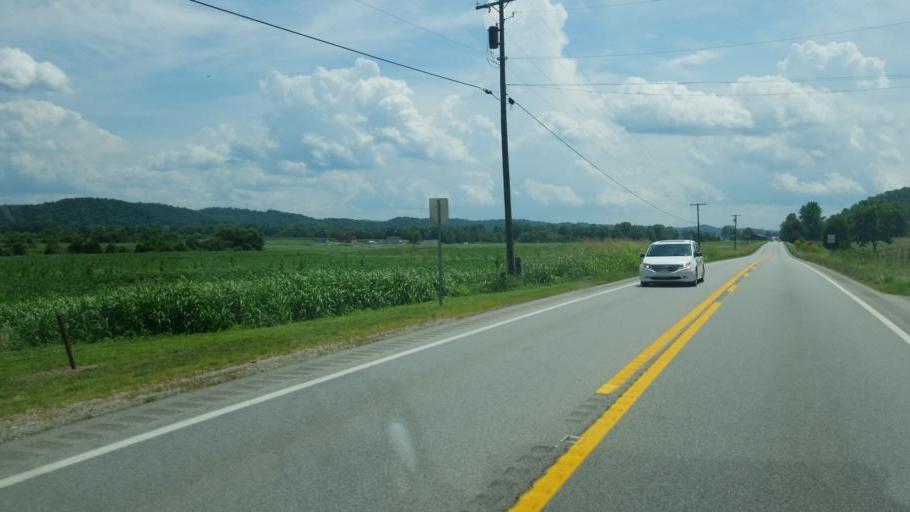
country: US
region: West Virginia
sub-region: Putnam County
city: Buffalo
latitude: 38.7268
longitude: -81.9720
